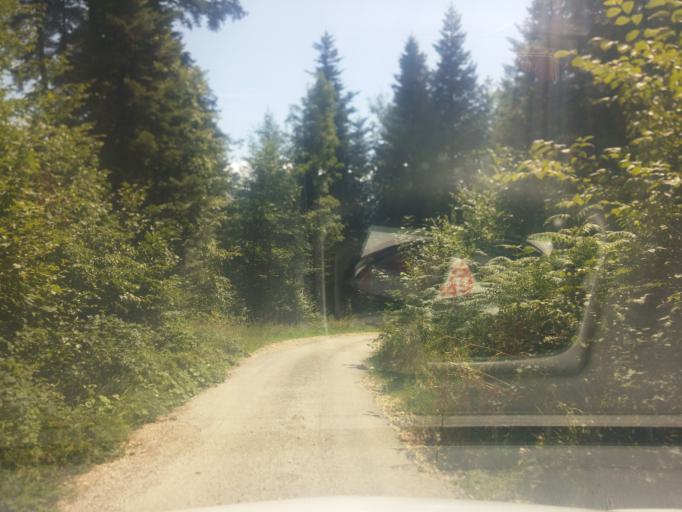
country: FR
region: Franche-Comte
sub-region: Departement du Jura
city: Saint-Lupicin
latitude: 46.4183
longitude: 5.7825
